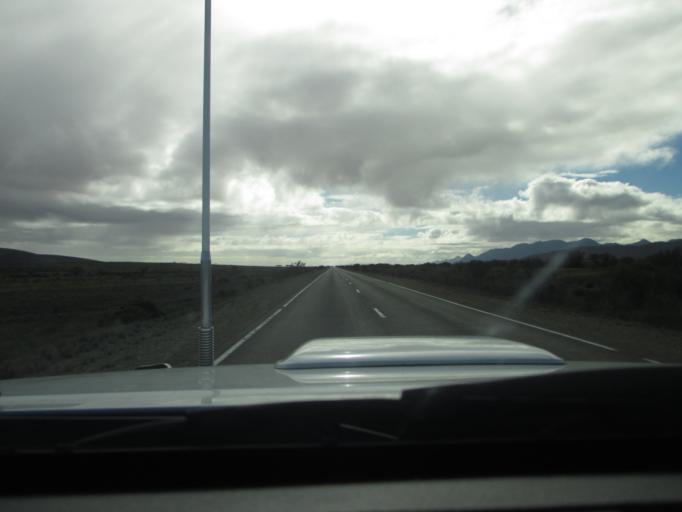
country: AU
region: South Australia
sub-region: Flinders Ranges
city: Quorn
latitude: -31.6436
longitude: 138.3830
